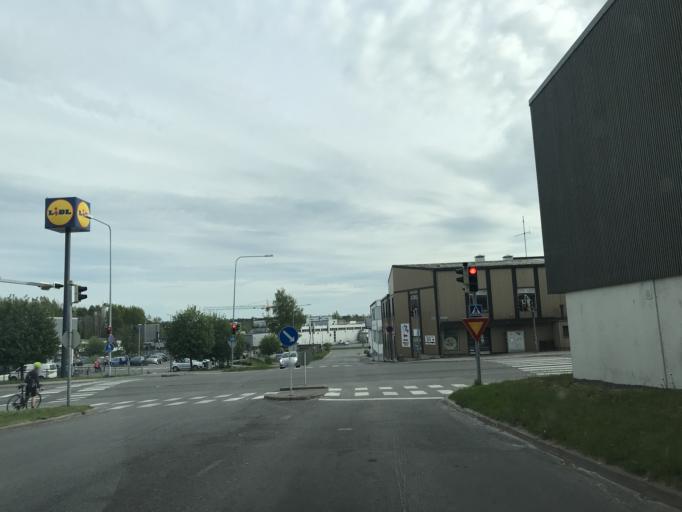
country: FI
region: Varsinais-Suomi
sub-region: Turku
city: Turku
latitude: 60.4504
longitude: 22.3088
